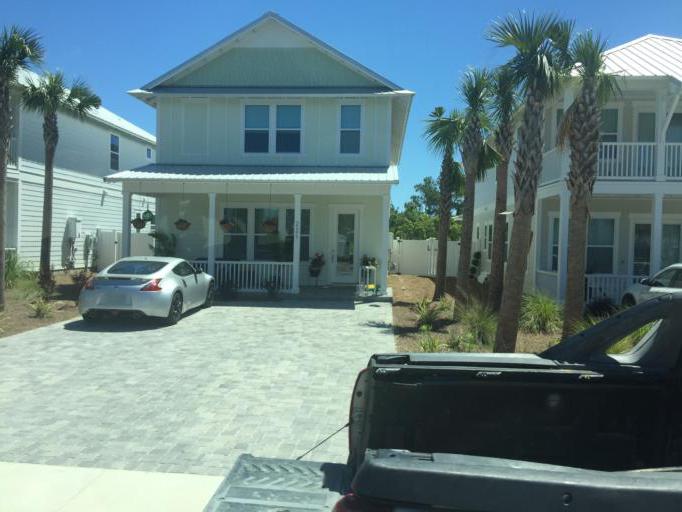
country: US
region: Florida
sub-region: Bay County
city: Laguna Beach
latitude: 30.2353
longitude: -85.9111
